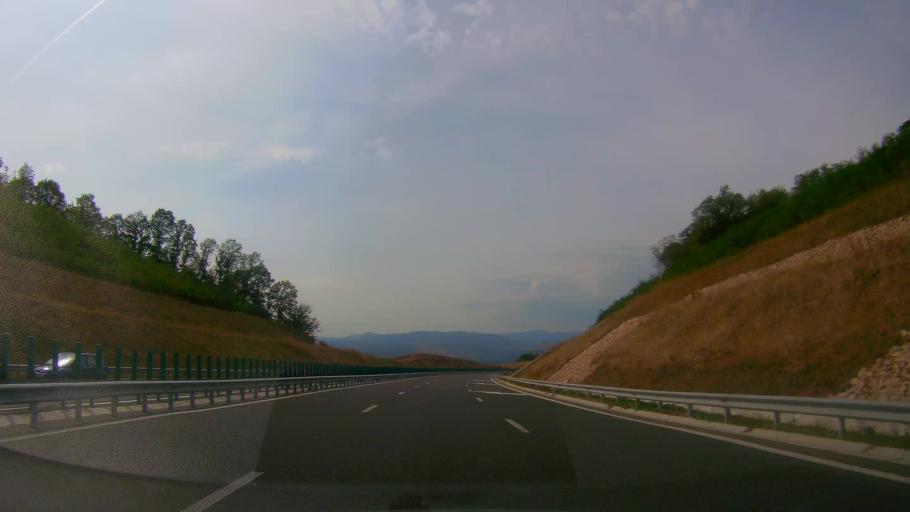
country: RO
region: Cluj
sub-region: Comuna Floresti
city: Luna de Sus
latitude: 46.7817
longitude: 23.4152
